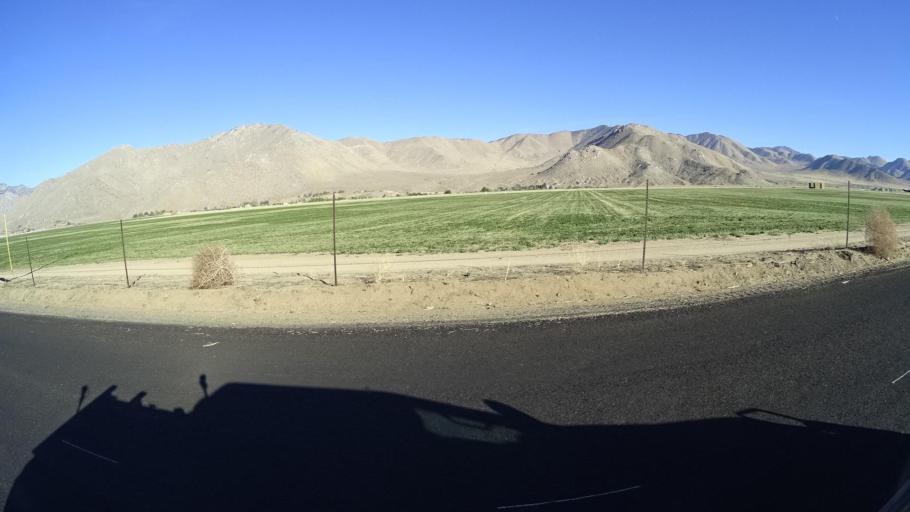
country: US
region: California
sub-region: Kern County
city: Weldon
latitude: 35.6314
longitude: -118.2629
